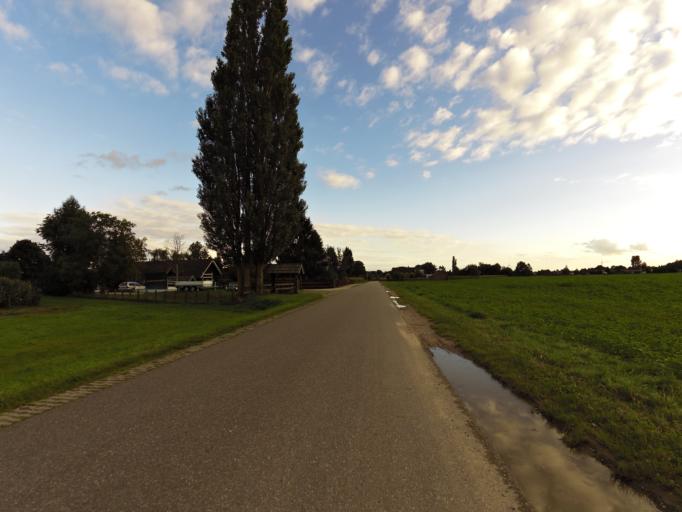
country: NL
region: Gelderland
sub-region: Gemeente Montferland
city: s-Heerenberg
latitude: 51.8892
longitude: 6.2646
